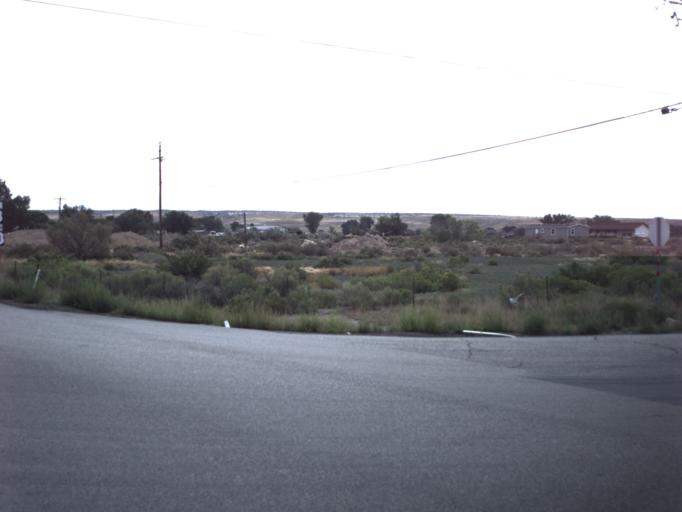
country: US
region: Utah
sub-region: Carbon County
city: Wellington
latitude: 39.5425
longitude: -110.6932
